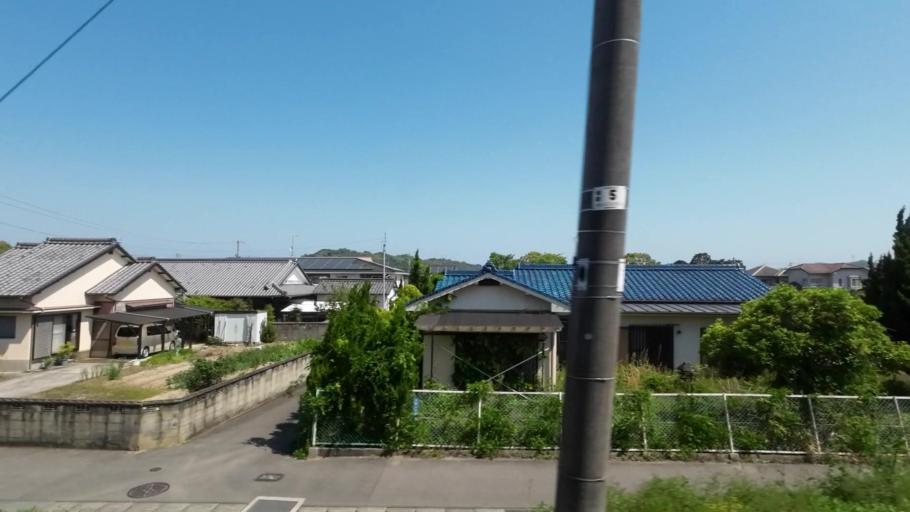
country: JP
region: Ehime
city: Niihama
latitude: 33.9706
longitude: 133.3269
